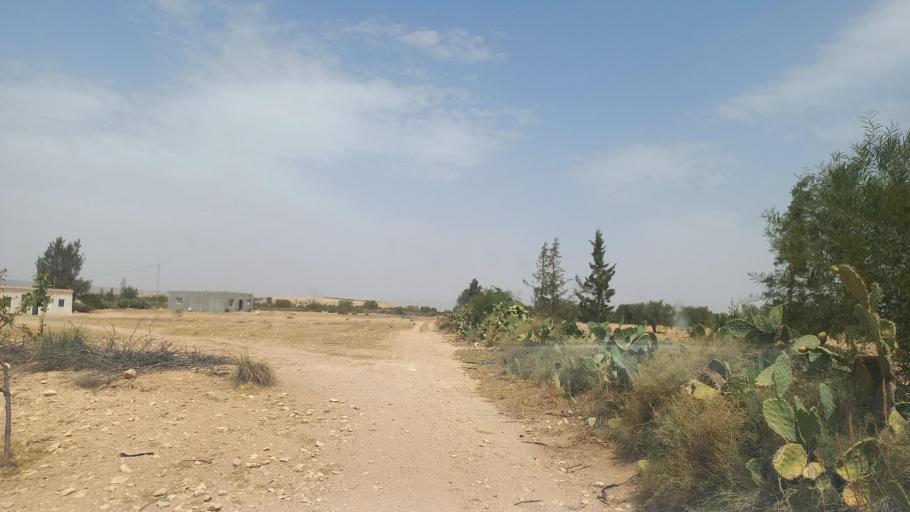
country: TN
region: Al Qasrayn
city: Kasserine
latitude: 35.2629
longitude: 8.9865
